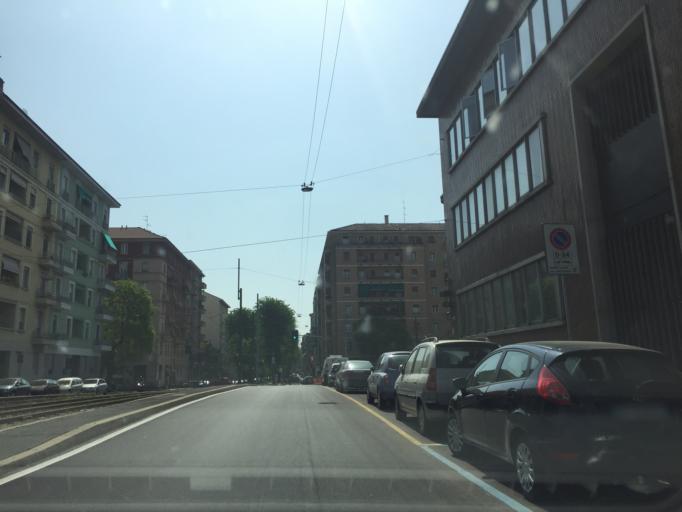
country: IT
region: Lombardy
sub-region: Citta metropolitana di Milano
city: Milano
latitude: 45.4918
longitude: 9.1605
